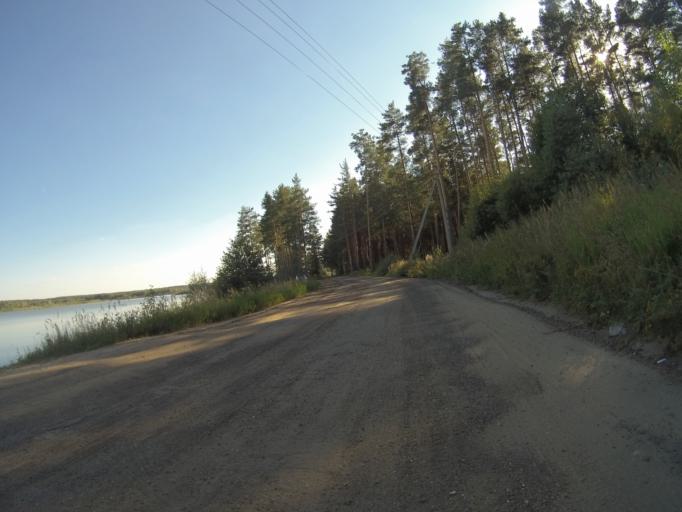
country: RU
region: Vladimir
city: Kommunar
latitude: 56.0521
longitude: 40.4138
